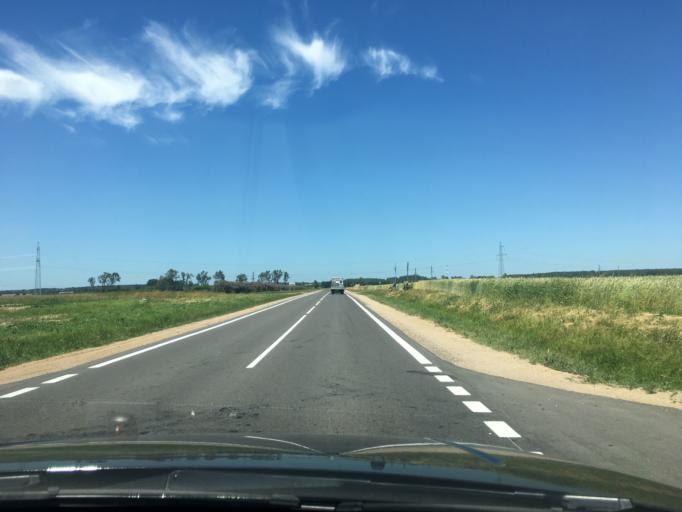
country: BY
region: Grodnenskaya
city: Hal'shany
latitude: 54.1012
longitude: 25.9139
